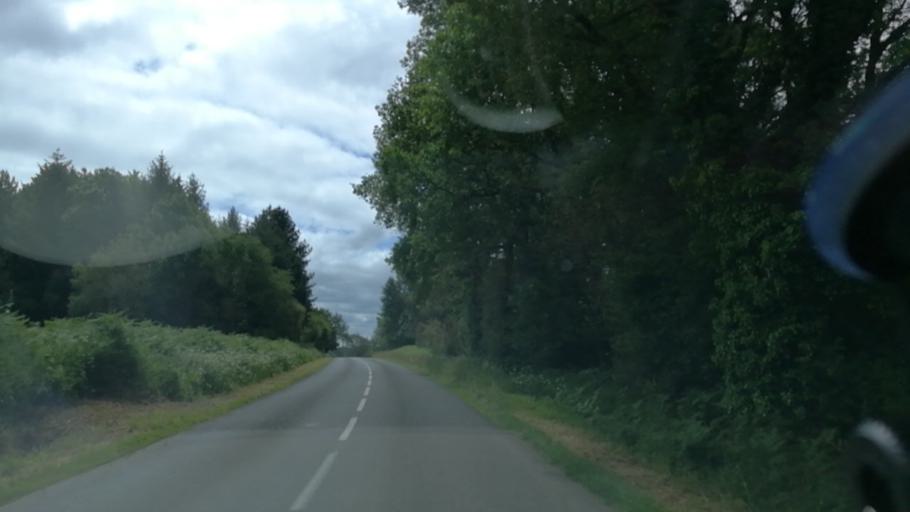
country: FR
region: Brittany
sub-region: Departement du Morbihan
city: Penestin
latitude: 47.4733
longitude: -2.4329
